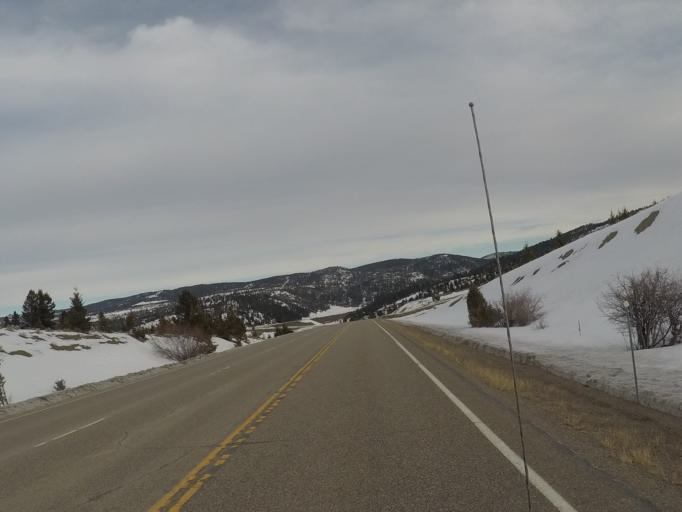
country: US
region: Montana
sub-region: Meagher County
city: White Sulphur Springs
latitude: 46.6590
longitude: -110.8734
